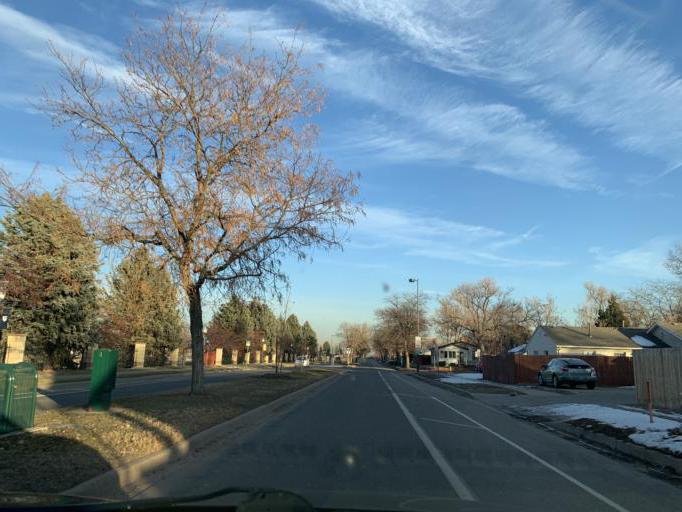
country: US
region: Colorado
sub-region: Adams County
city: Berkley
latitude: 39.7874
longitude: -105.0308
